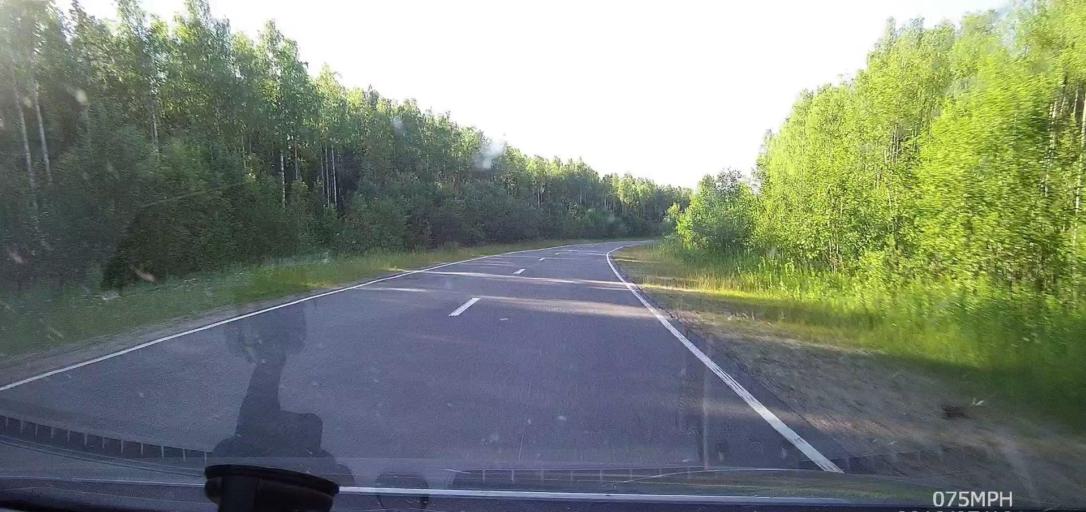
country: RU
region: Arkhangelskaya
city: Yemtsa
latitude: 63.2941
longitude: 40.5454
